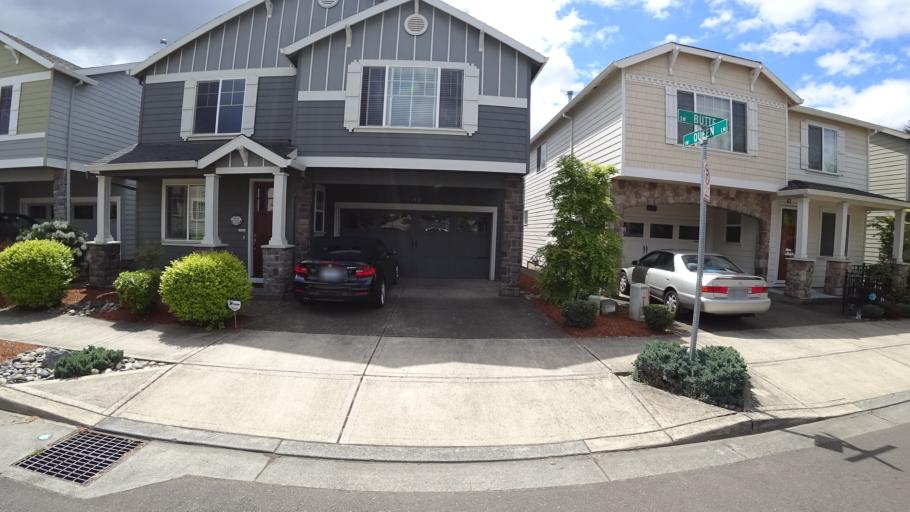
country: US
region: Oregon
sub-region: Washington County
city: Beaverton
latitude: 45.4678
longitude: -122.7958
